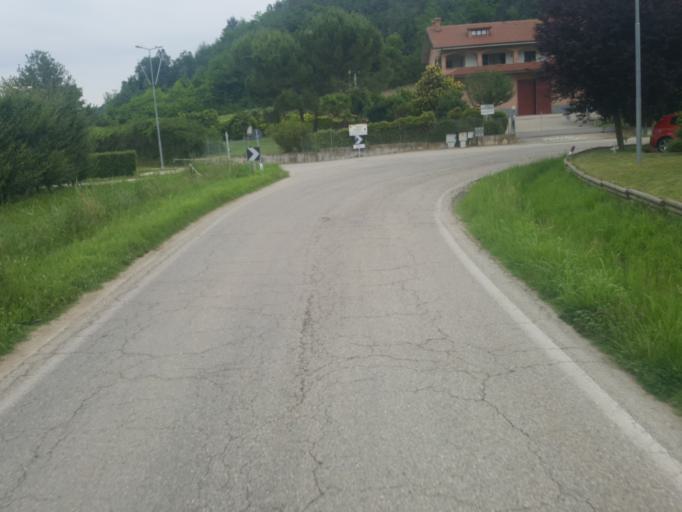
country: IT
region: Piedmont
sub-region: Provincia di Cuneo
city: Castellinaldo
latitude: 44.7676
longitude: 8.0207
